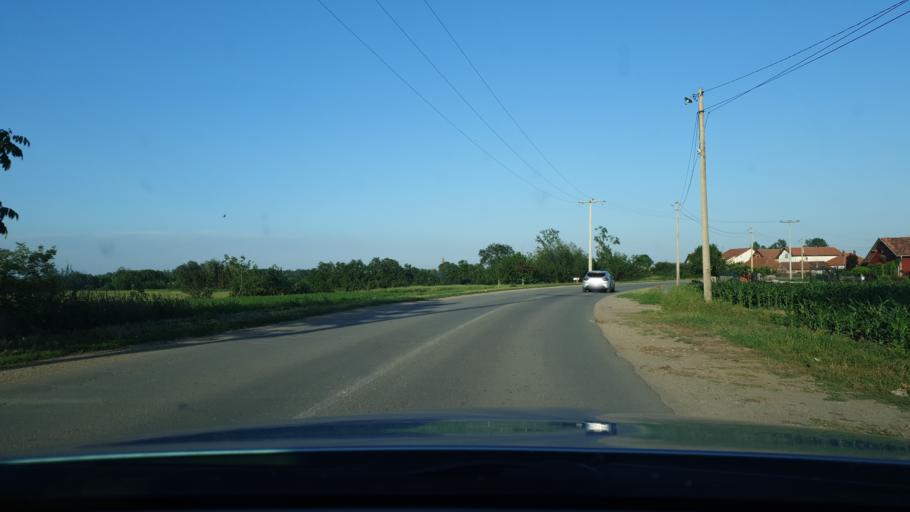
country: RS
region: Central Serbia
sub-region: Podunavski Okrug
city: Velika Plana
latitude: 44.3420
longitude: 21.0899
